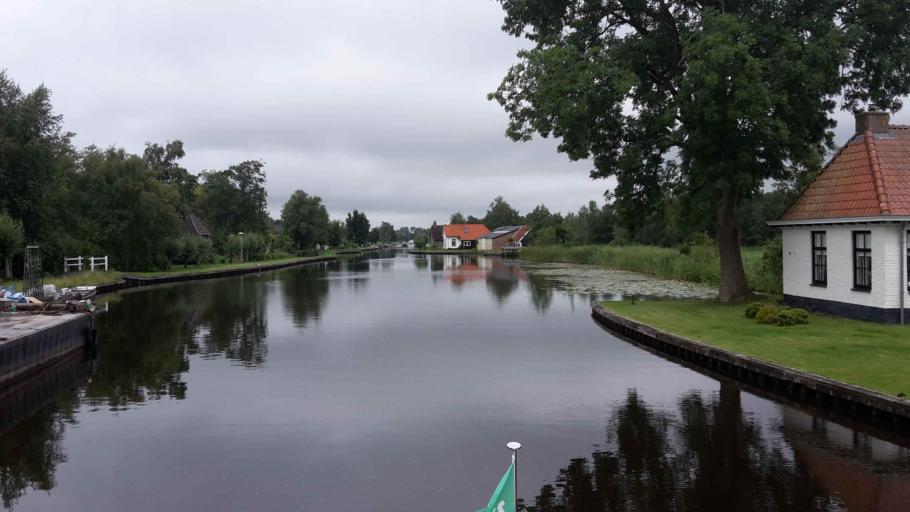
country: NL
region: Overijssel
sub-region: Gemeente Steenwijkerland
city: Oldemarkt
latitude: 52.7968
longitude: 5.9314
